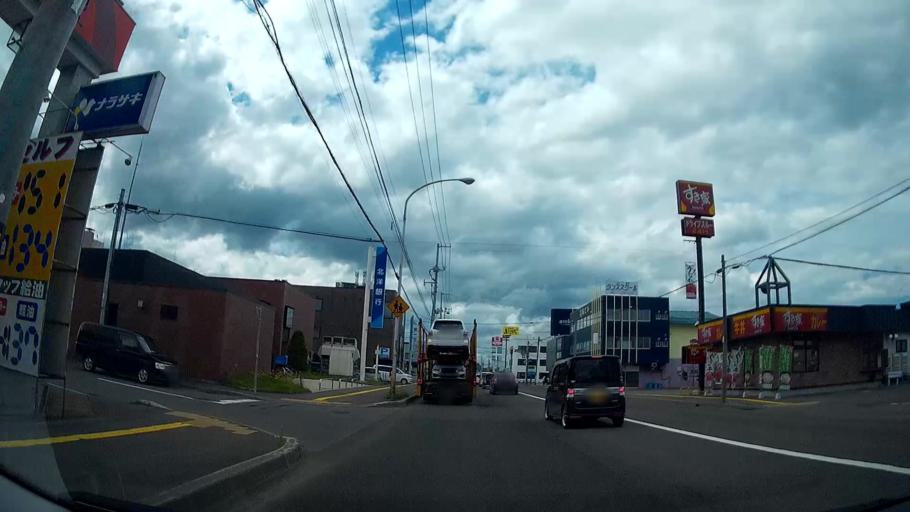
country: JP
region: Hokkaido
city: Kitahiroshima
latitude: 42.8806
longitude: 141.5777
